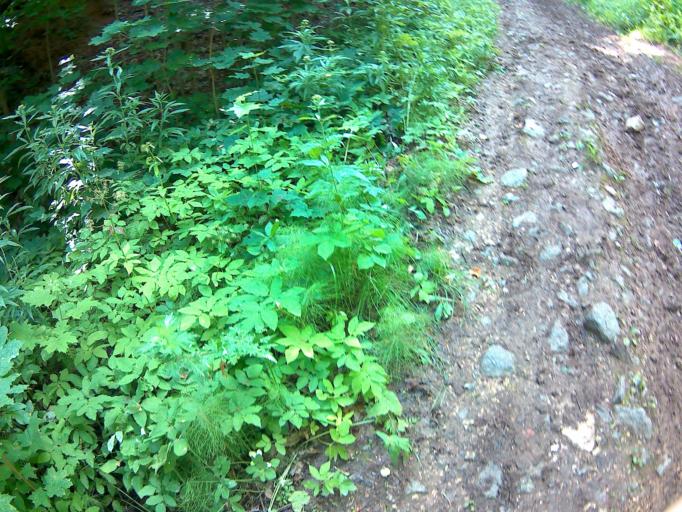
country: RU
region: Nizjnij Novgorod
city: Nizhniy Novgorod
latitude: 56.2407
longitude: 43.9399
